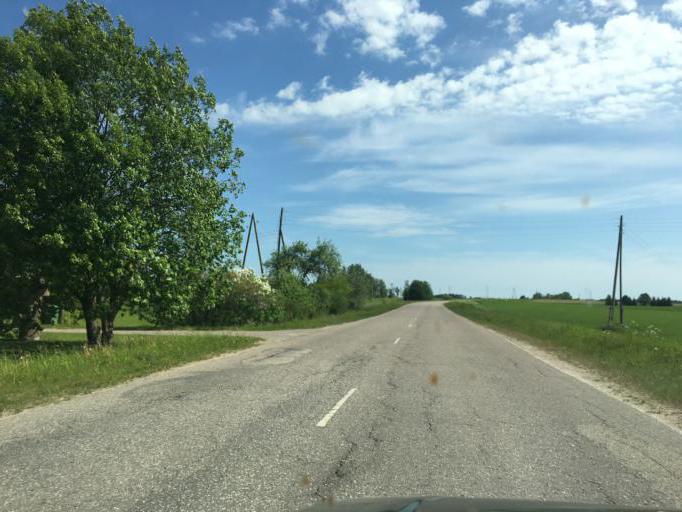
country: LV
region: Talsu Rajons
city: Valdemarpils
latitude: 57.3757
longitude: 22.5058
